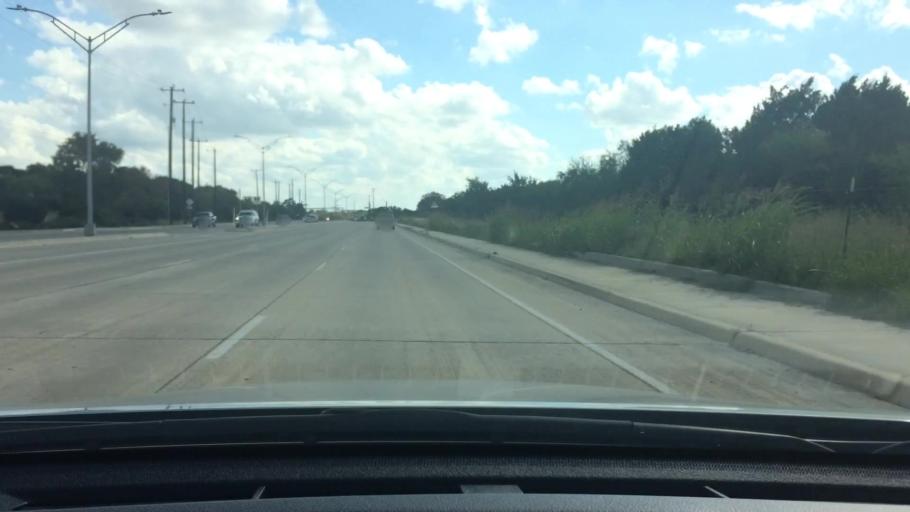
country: US
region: Texas
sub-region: Bexar County
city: Hollywood Park
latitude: 29.6201
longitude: -98.4231
